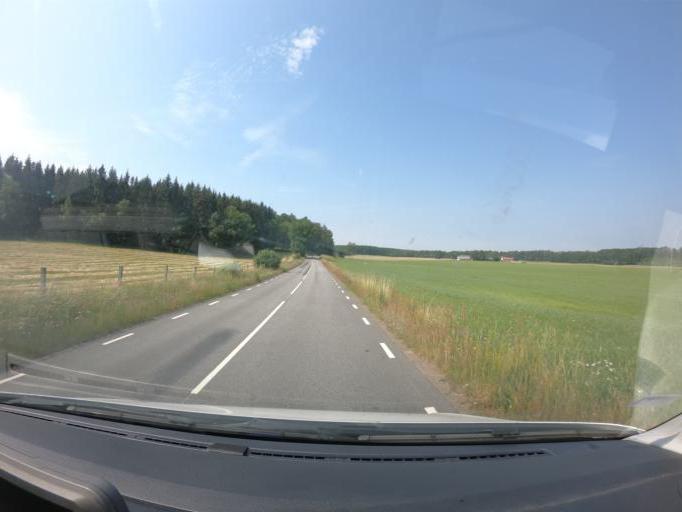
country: SE
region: Skane
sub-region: Hassleholms Kommun
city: Tormestorp
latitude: 56.1550
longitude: 13.6461
